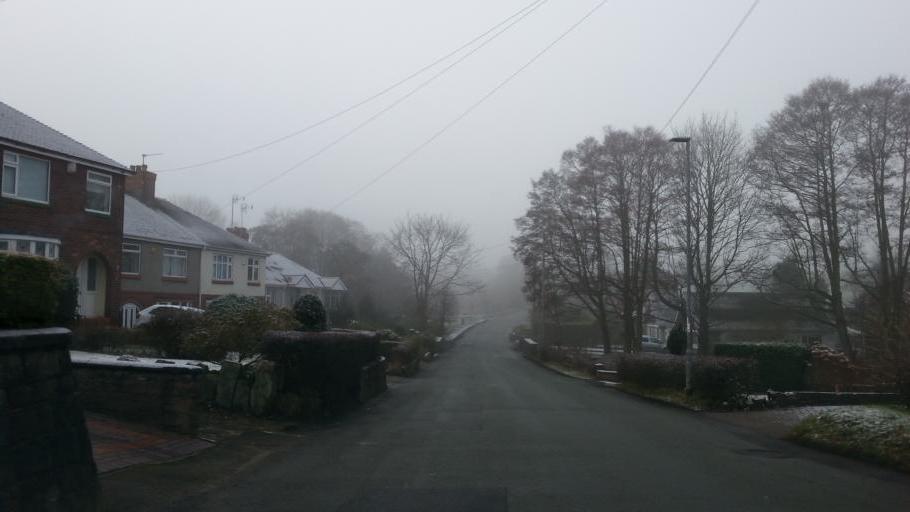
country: GB
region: England
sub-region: Staffordshire
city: Biddulph
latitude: 53.1234
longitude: -2.1707
